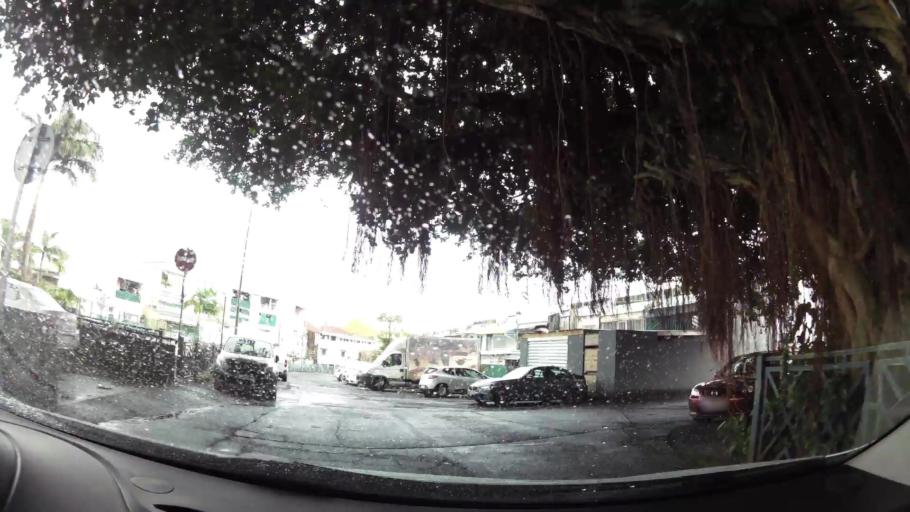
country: RE
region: Reunion
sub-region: Reunion
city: Saint-Andre
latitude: -20.9601
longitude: 55.6508
